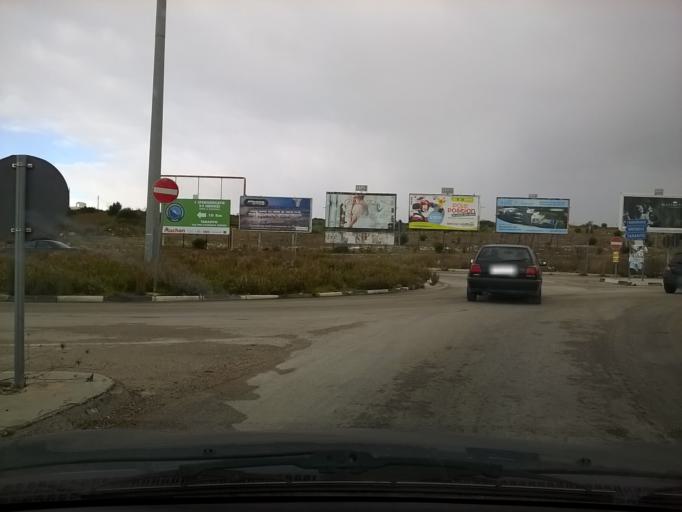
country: IT
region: Apulia
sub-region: Provincia di Taranto
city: Paolo VI
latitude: 40.5186
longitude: 17.2874
